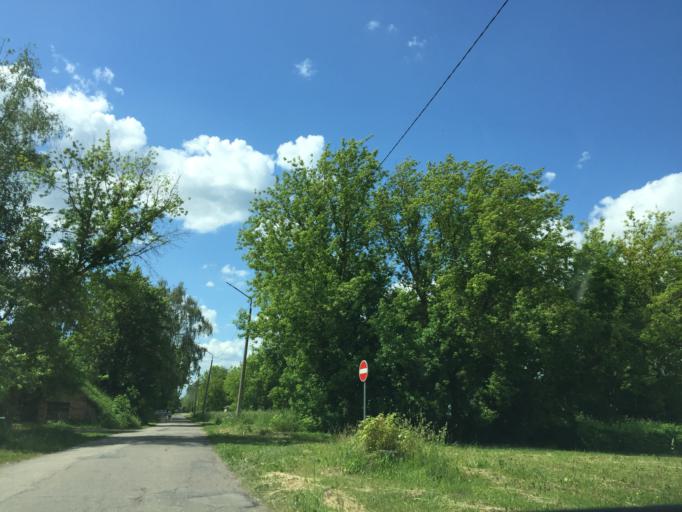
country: LV
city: Tireli
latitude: 56.8040
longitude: 23.6010
